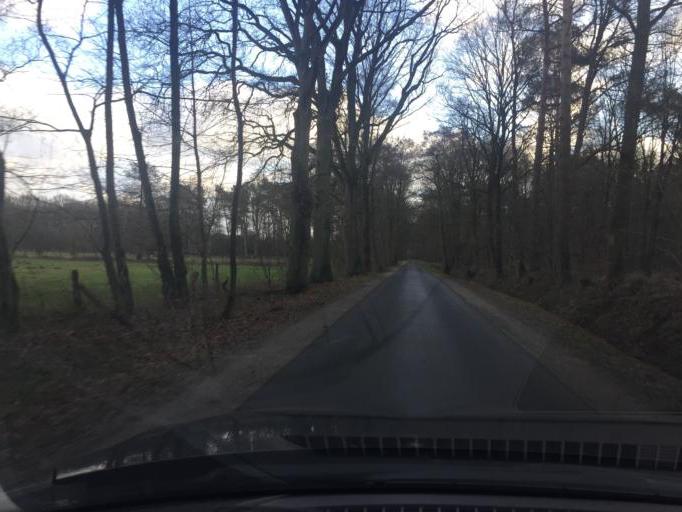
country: DE
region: North Rhine-Westphalia
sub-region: Regierungsbezirk Dusseldorf
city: Schermbeck
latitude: 51.7007
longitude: 6.8532
